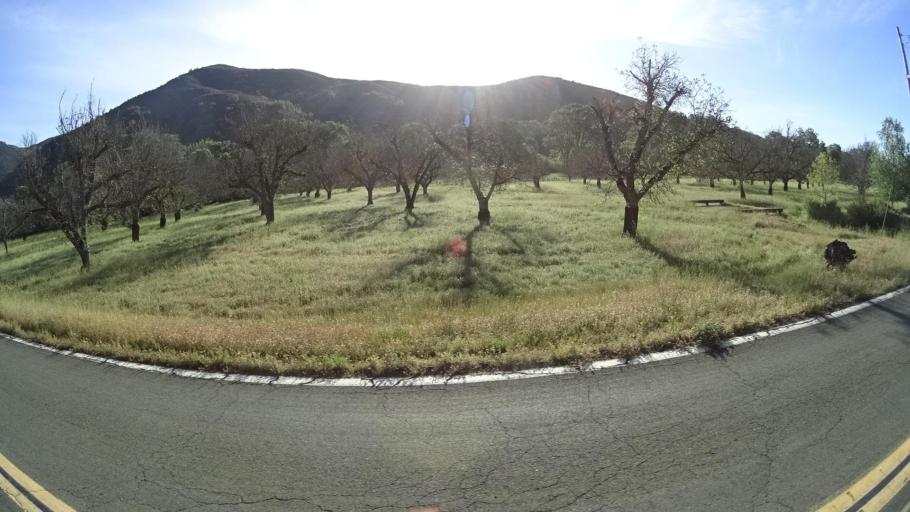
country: US
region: California
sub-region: Lake County
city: Upper Lake
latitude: 39.1291
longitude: -122.9968
